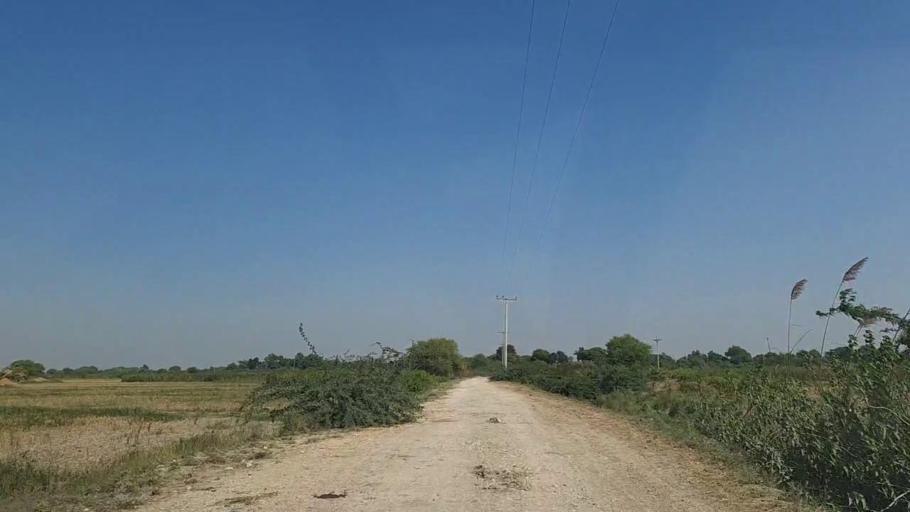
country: PK
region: Sindh
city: Daro Mehar
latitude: 24.7232
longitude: 68.1781
